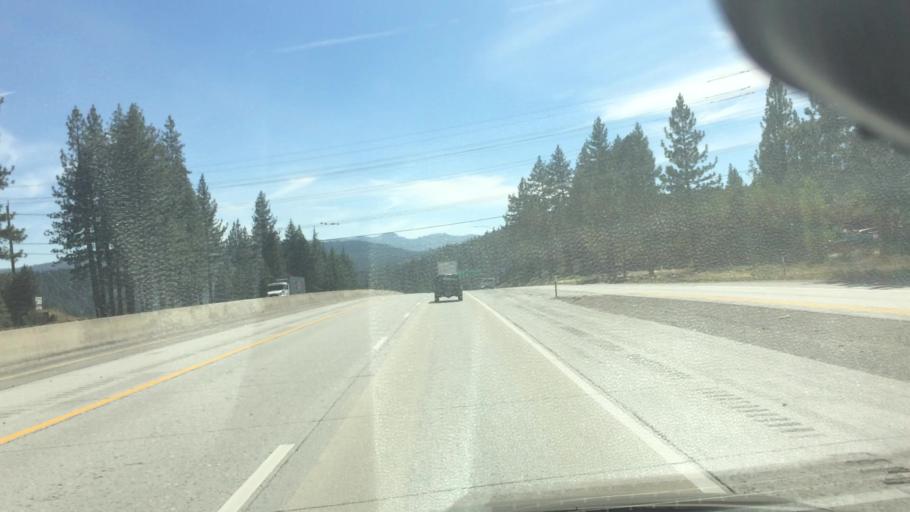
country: US
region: California
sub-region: Nevada County
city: Truckee
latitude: 39.3339
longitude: -120.1814
